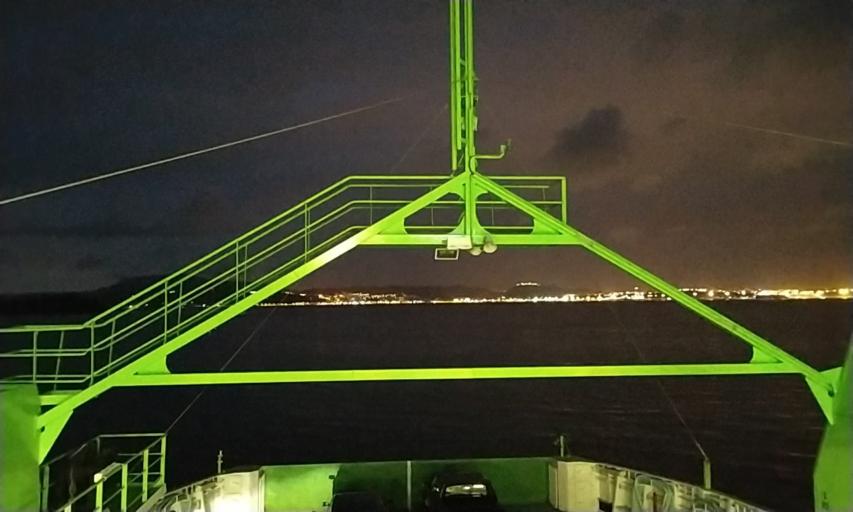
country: PT
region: Setubal
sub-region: Setubal
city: Setubal
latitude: 38.4776
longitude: -8.8691
